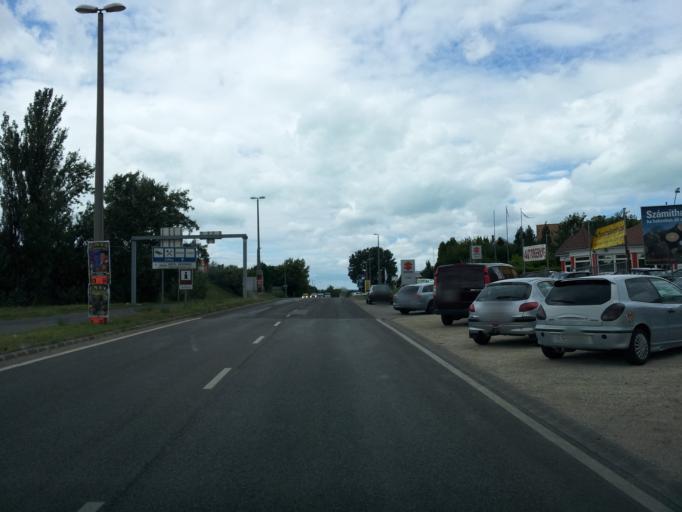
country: HU
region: Somogy
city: Siofok
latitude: 46.8962
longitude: 18.0551
